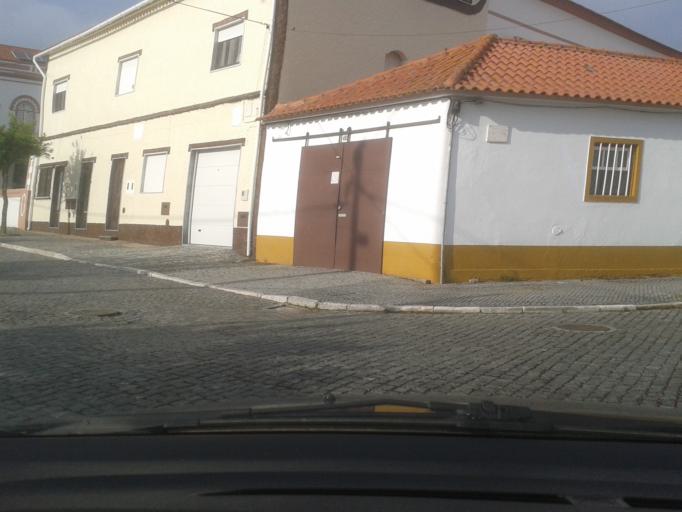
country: PT
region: Portalegre
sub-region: Avis
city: Avis
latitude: 39.0524
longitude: -7.8913
